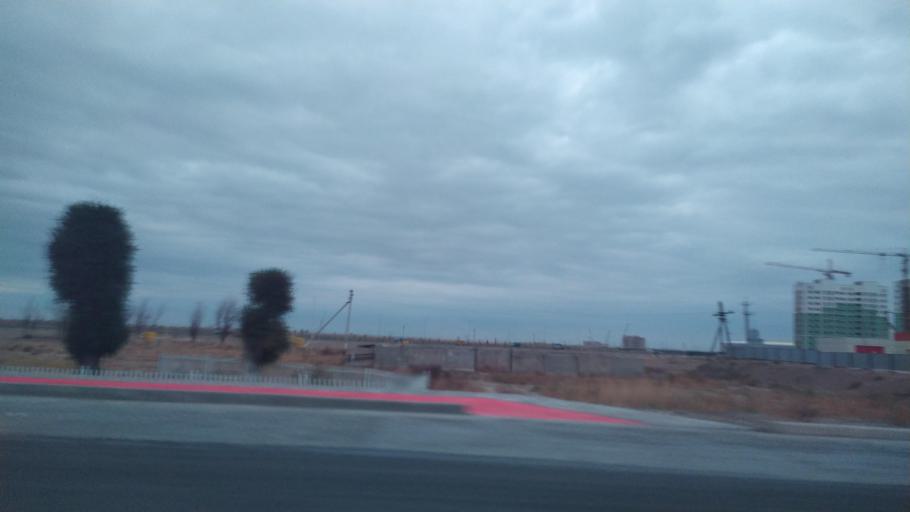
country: KZ
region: Ongtustik Qazaqstan
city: Turkestan
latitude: 43.2696
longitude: 68.3517
